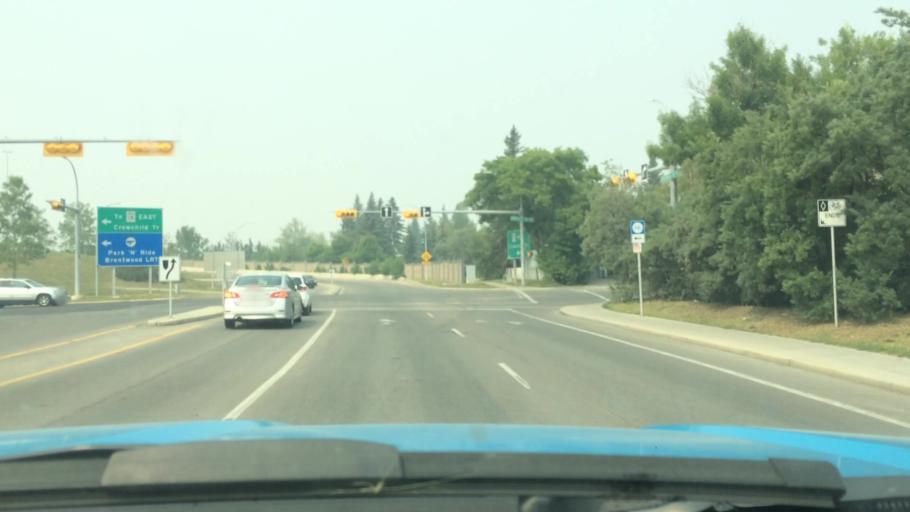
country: CA
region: Alberta
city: Calgary
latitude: 51.0893
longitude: -114.1330
